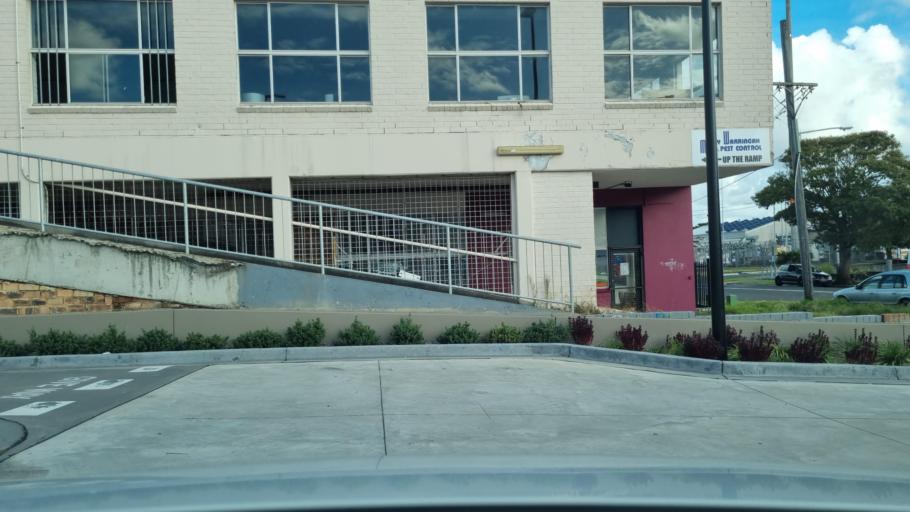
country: AU
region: New South Wales
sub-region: Warringah
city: Brookvale
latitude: -33.7617
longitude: 151.2751
